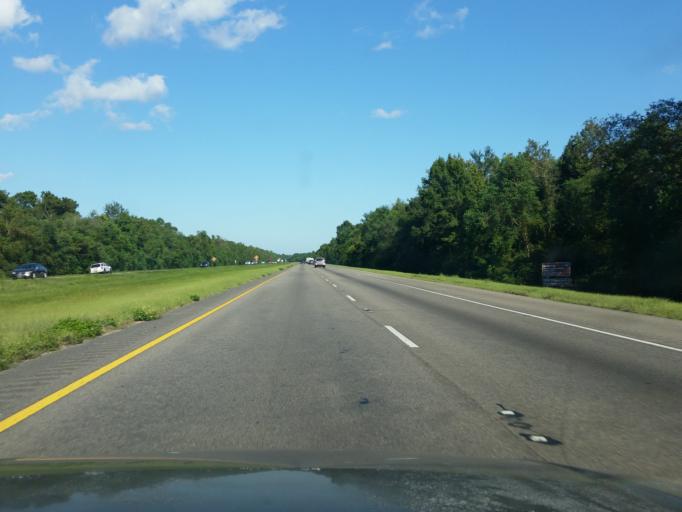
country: US
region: Mississippi
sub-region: Hancock County
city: Pearlington
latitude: 30.2971
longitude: -89.6887
